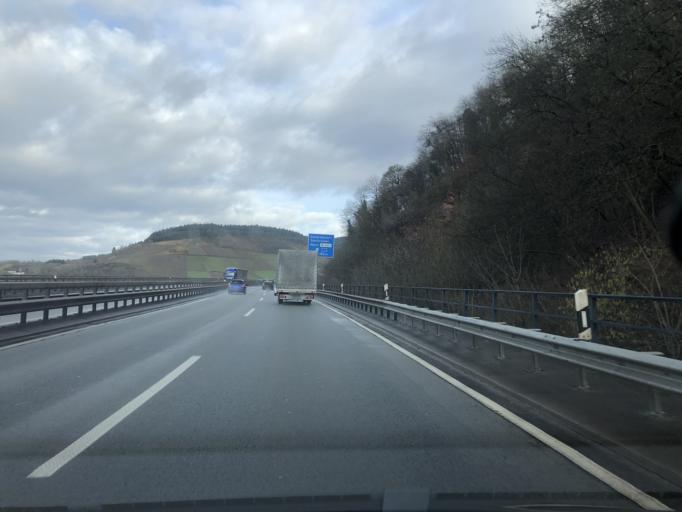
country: DE
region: Rheinland-Pfalz
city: Schweich
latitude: 49.8118
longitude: 6.7491
